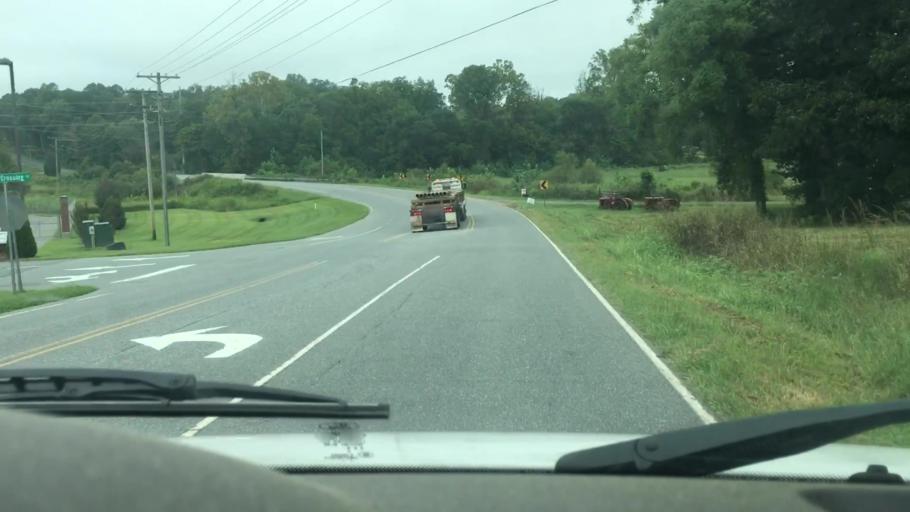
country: US
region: North Carolina
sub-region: Gaston County
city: Davidson
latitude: 35.5193
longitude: -80.8136
